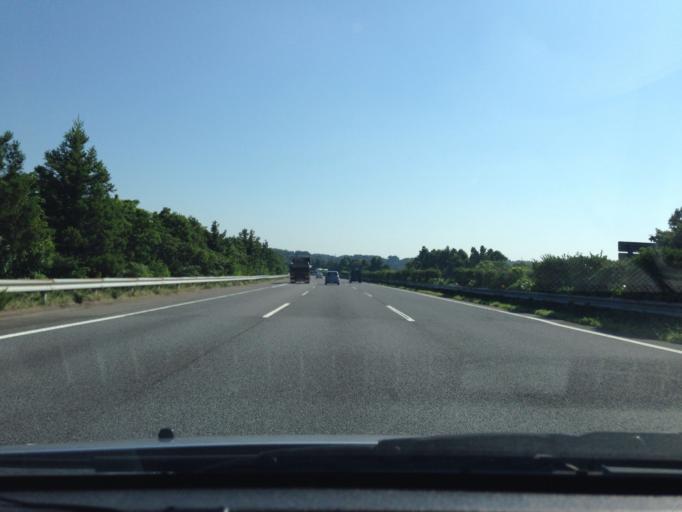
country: JP
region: Ibaraki
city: Naka
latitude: 36.0980
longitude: 140.1704
